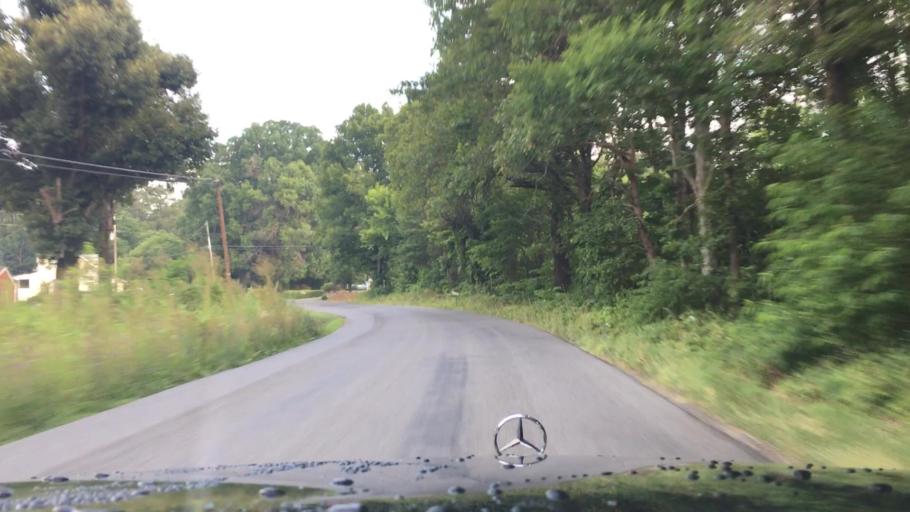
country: US
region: Virginia
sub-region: Campbell County
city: Altavista
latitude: 37.1472
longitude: -79.2916
